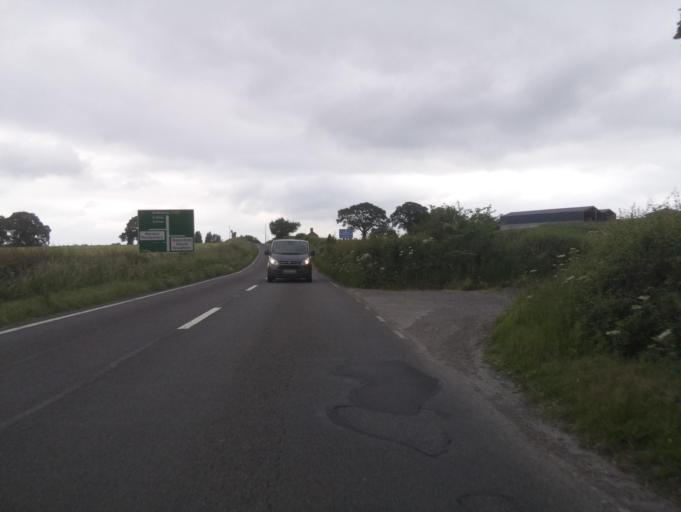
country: GB
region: England
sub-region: Derbyshire
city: Rodsley
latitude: 52.9140
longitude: -1.7606
